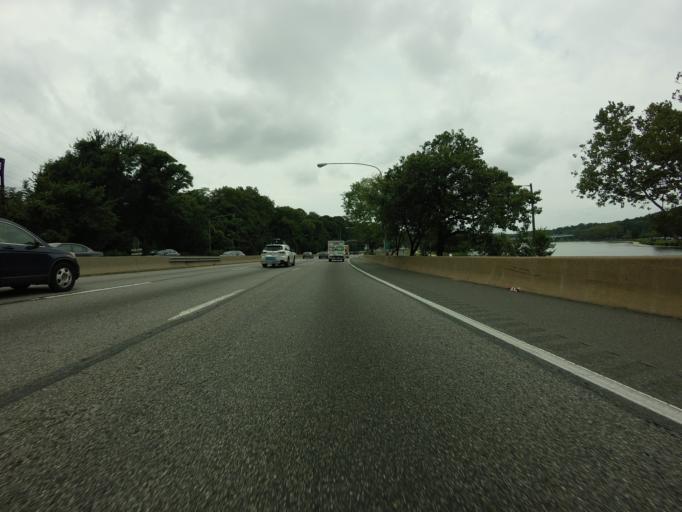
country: US
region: Pennsylvania
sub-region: Philadelphia County
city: Philadelphia
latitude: 39.9681
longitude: -75.1902
